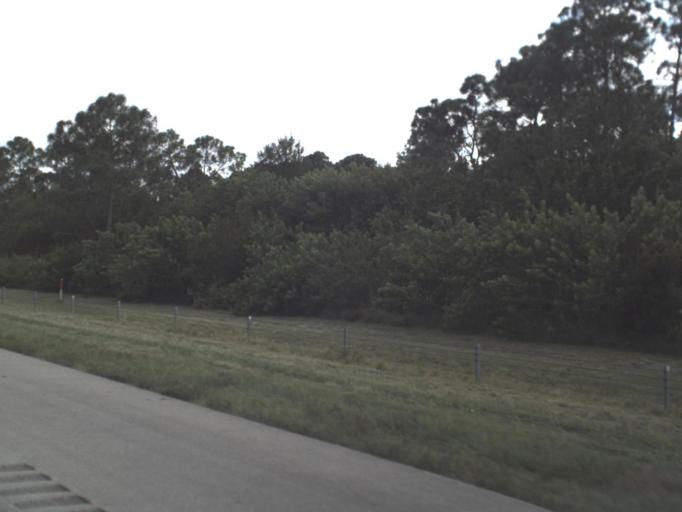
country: US
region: Florida
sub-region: Saint Lucie County
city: Lakewood Park
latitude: 27.4626
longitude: -80.4354
